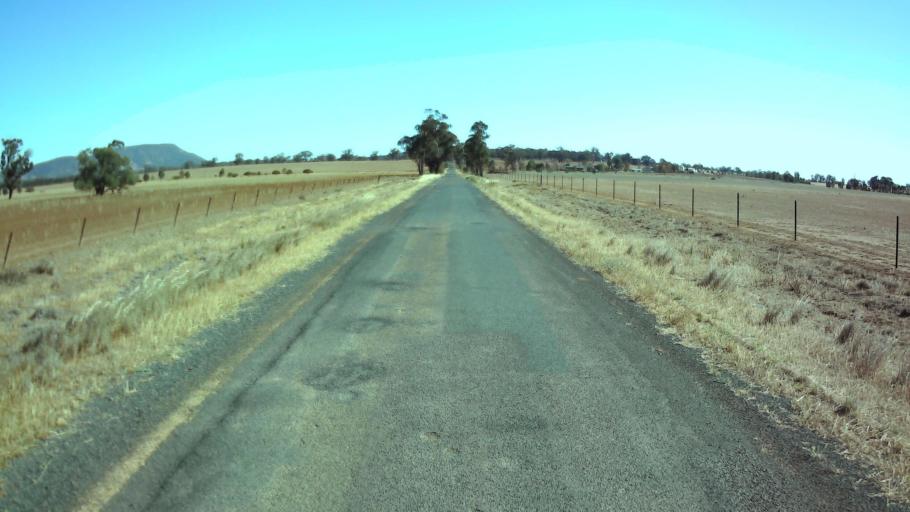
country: AU
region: New South Wales
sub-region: Weddin
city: Grenfell
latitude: -33.7979
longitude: 147.9563
